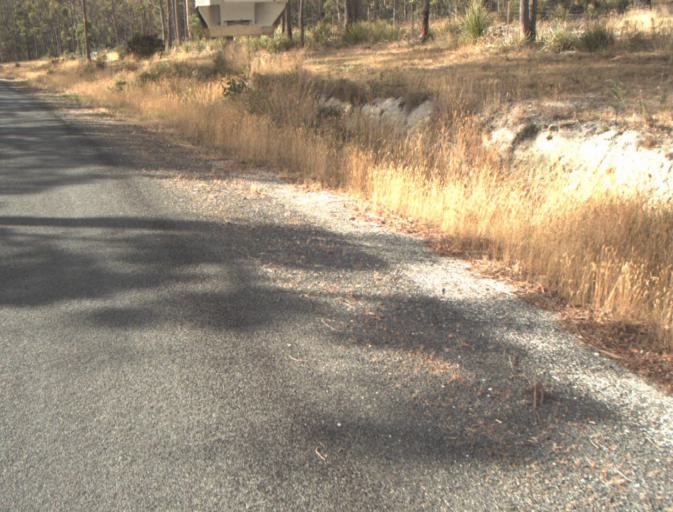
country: AU
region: Tasmania
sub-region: Dorset
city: Bridport
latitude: -41.1144
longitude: 147.2017
